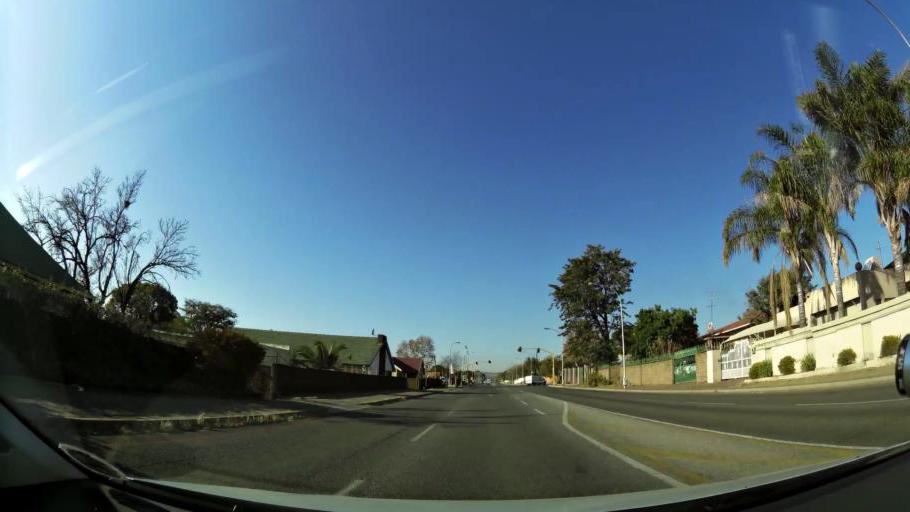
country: ZA
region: Gauteng
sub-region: City of Johannesburg Metropolitan Municipality
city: Modderfontein
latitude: -26.1378
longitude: 28.1581
